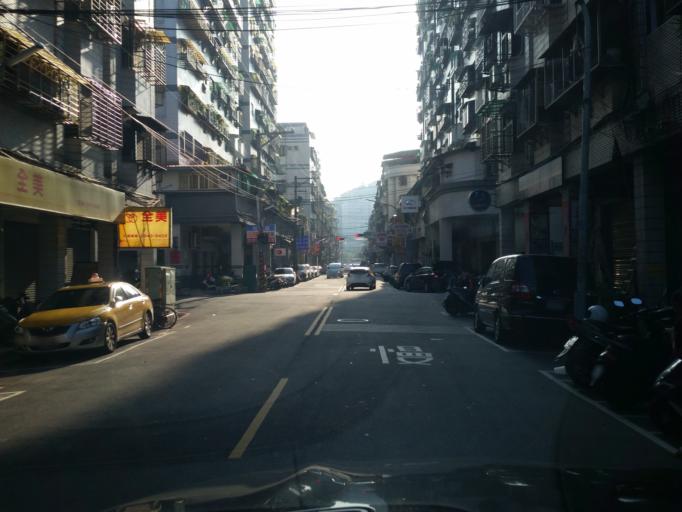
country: TW
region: Taipei
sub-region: Taipei
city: Banqiao
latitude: 24.9867
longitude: 121.5214
